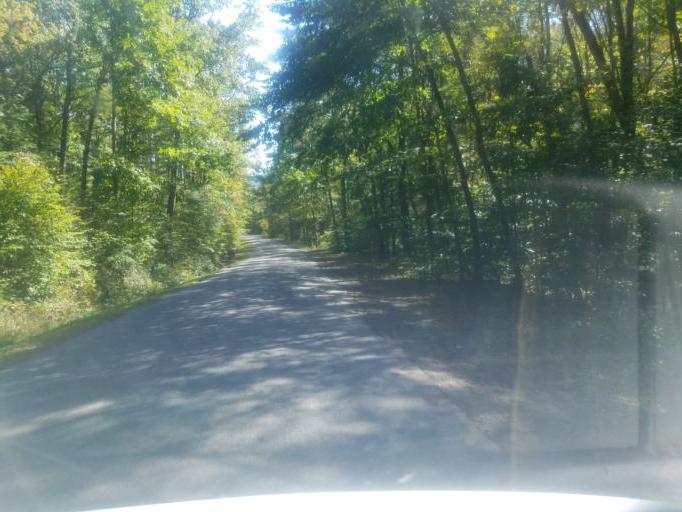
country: US
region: New York
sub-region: Allegany County
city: Cuba
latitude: 42.3087
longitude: -78.2027
